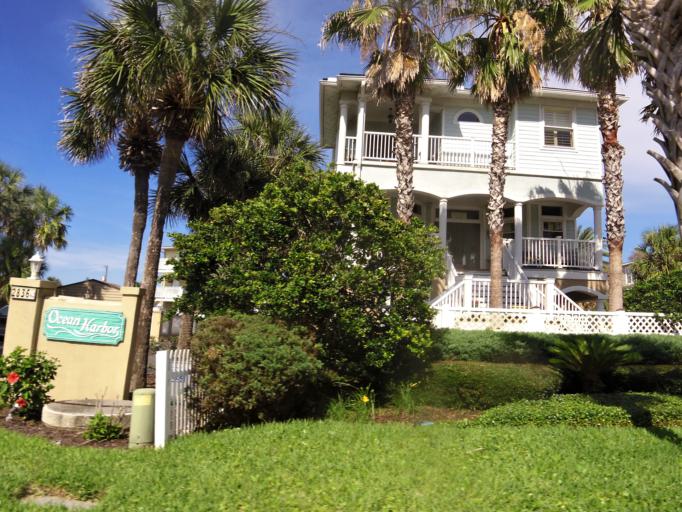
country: US
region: Florida
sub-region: Saint Johns County
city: Villano Beach
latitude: 29.9178
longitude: -81.2926
